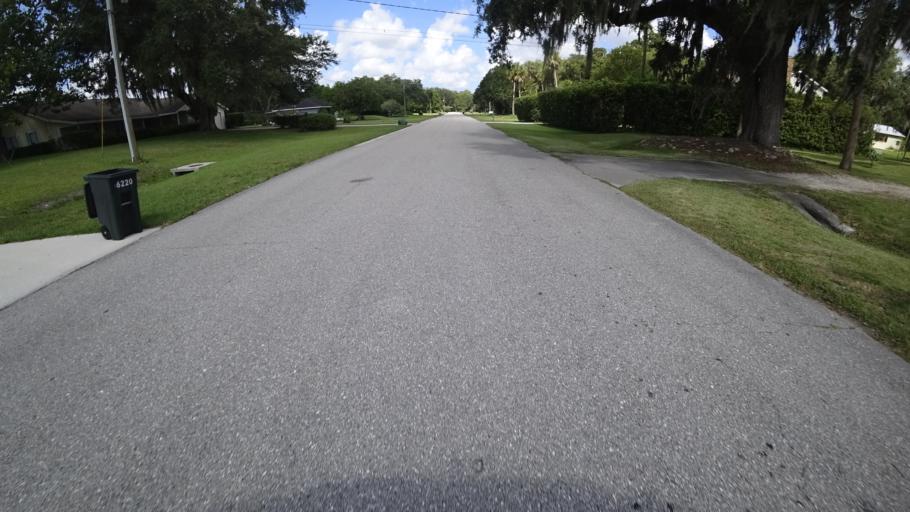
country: US
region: Florida
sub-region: Manatee County
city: Samoset
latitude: 27.4755
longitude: -82.4815
